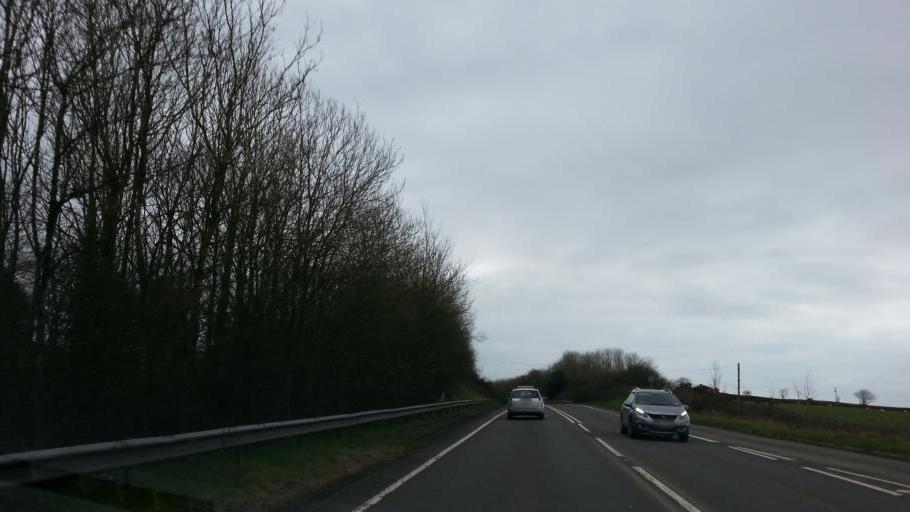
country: GB
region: England
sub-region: Devon
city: Fremington
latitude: 51.0418
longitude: -4.1353
